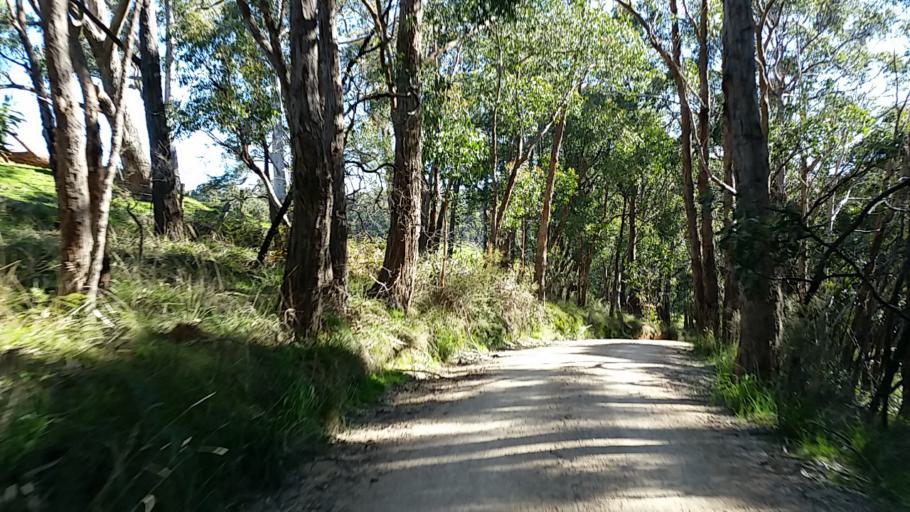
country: AU
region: South Australia
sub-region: Adelaide Hills
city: Lobethal
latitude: -34.8883
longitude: 138.8531
